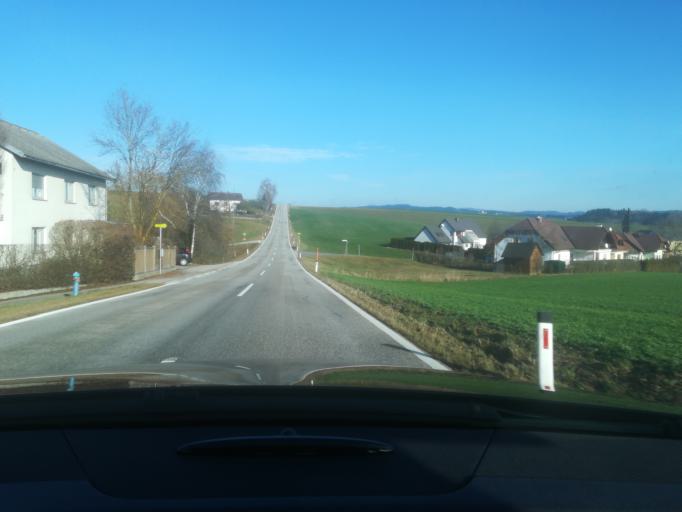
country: AT
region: Upper Austria
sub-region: Politischer Bezirk Urfahr-Umgebung
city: Herzogsdorf
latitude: 48.4090
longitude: 14.0859
